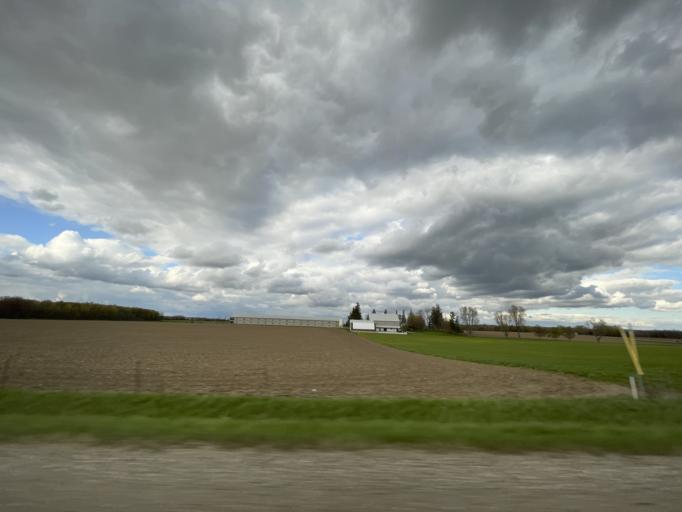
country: CA
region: Ontario
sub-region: Wellington County
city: Guelph
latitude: 43.5104
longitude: -80.3120
